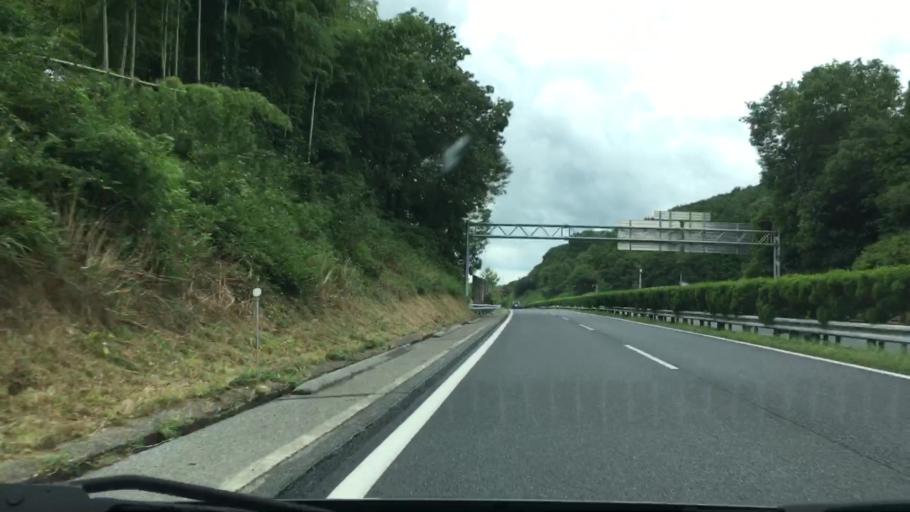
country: JP
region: Okayama
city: Tsuyama
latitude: 35.0407
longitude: 134.1256
